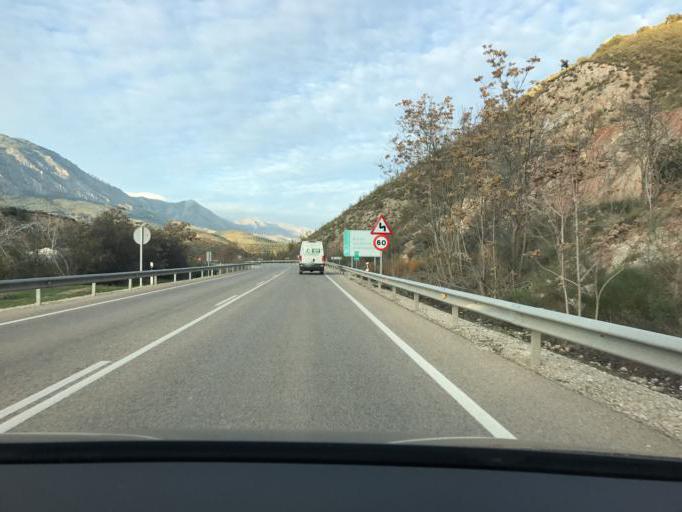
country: ES
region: Andalusia
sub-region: Provincia de Jaen
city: Huelma
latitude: 37.6603
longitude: -3.4178
